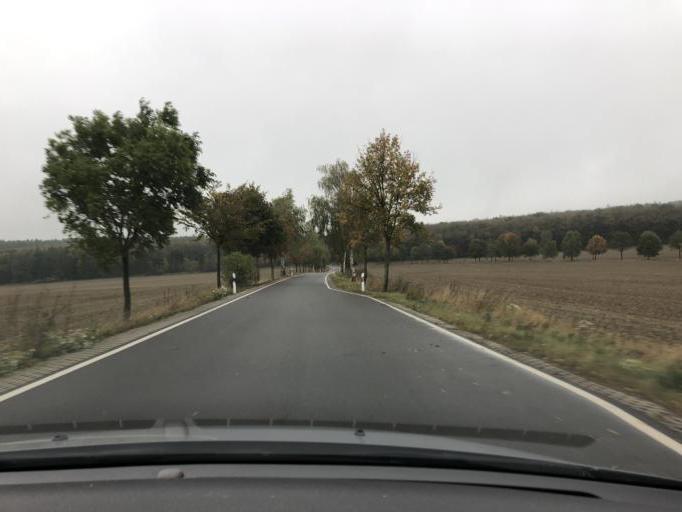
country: DE
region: Thuringia
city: Kreuzebra
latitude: 51.3547
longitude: 10.2624
